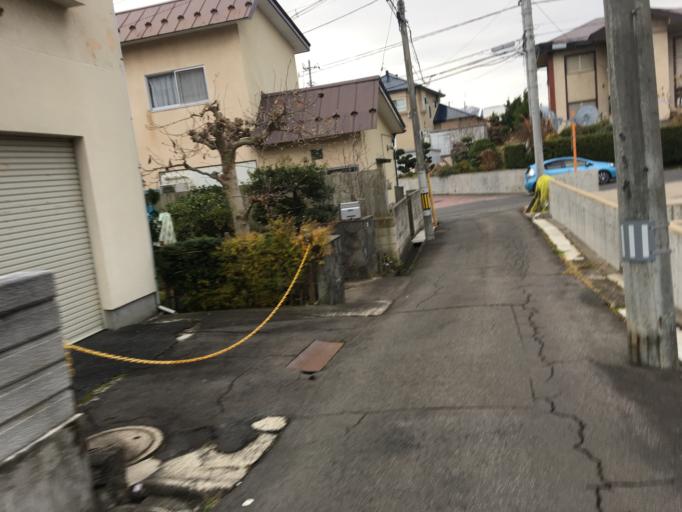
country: JP
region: Aomori
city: Hirosaki
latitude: 40.5930
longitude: 140.4663
